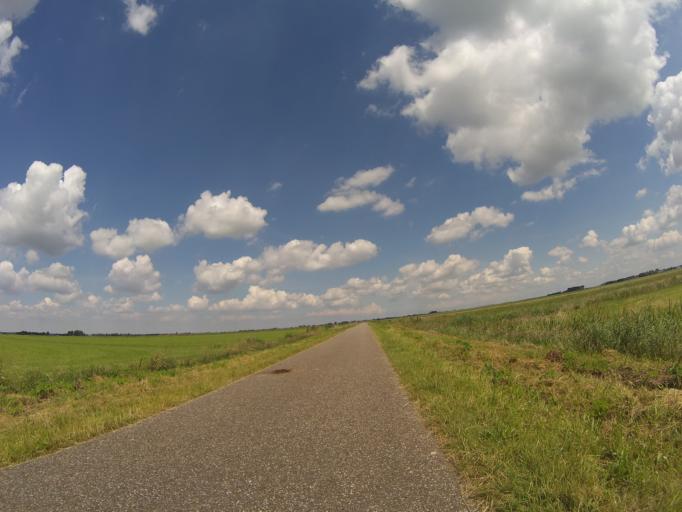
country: NL
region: Utrecht
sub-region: Gemeente Bunschoten
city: Spakenburg
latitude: 52.2303
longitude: 5.3326
